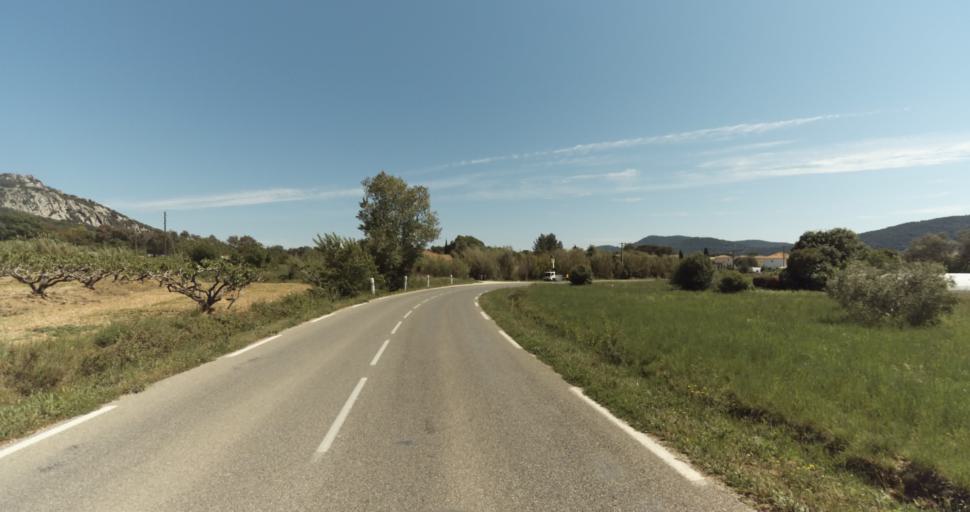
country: FR
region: Provence-Alpes-Cote d'Azur
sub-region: Departement du Var
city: La Crau
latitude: 43.1335
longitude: 6.0772
